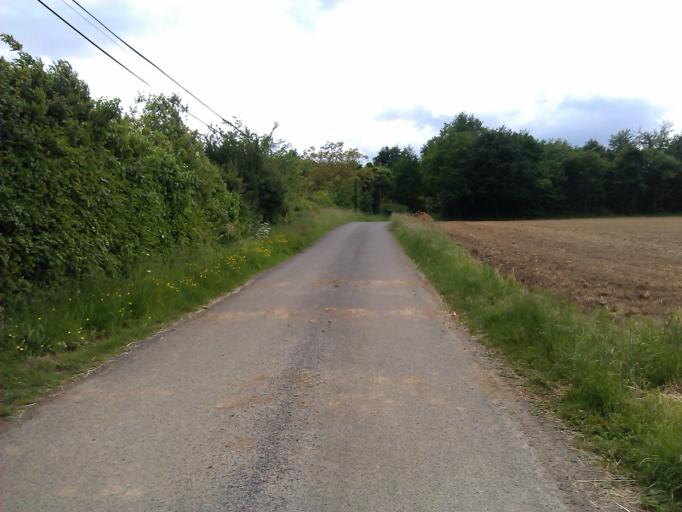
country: FR
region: Poitou-Charentes
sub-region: Departement de la Charente
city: Nanteuil-en-Vallee
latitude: 45.9666
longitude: 0.3112
